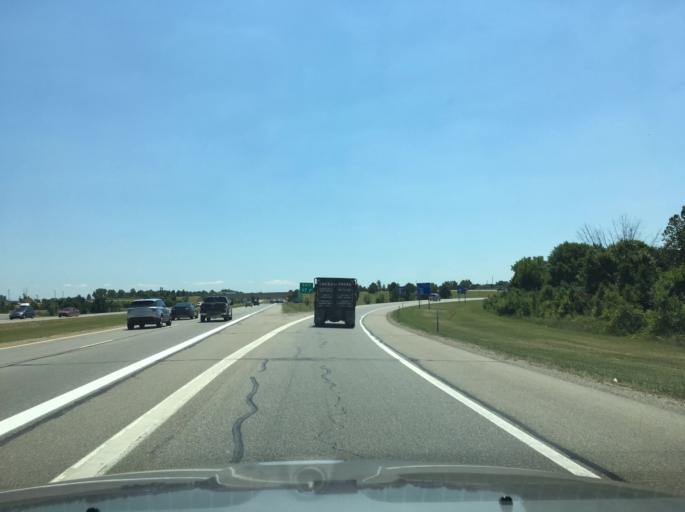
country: US
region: Michigan
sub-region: Macomb County
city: Utica
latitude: 42.6303
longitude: -83.0133
